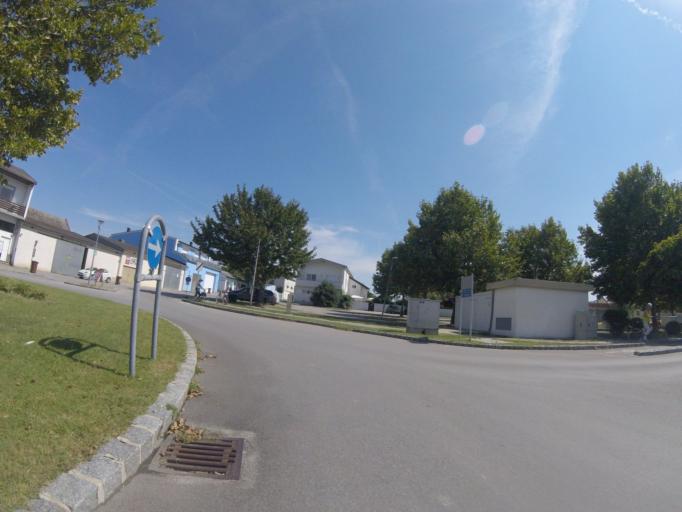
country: AT
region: Burgenland
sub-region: Politischer Bezirk Neusiedl am See
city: Podersdorf am See
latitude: 47.8578
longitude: 16.8298
